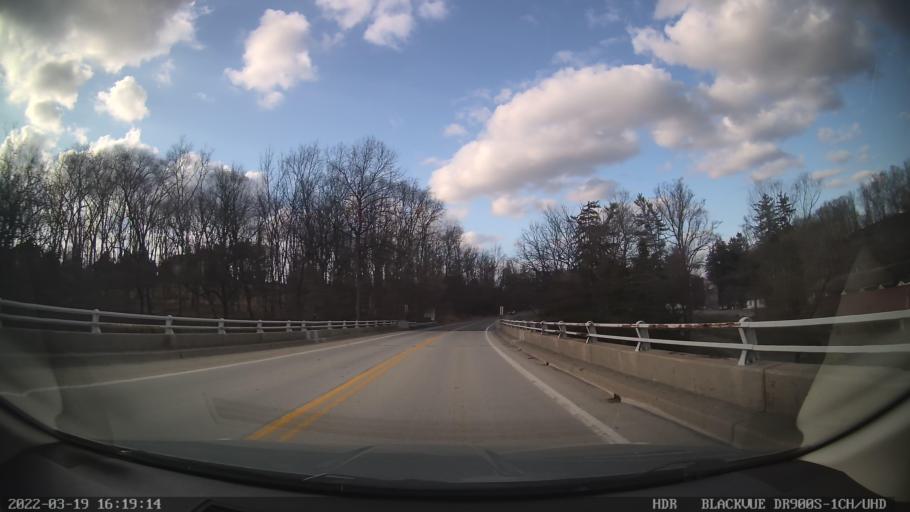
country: US
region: Pennsylvania
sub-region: Lehigh County
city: Dorneyville
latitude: 40.5687
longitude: -75.4990
